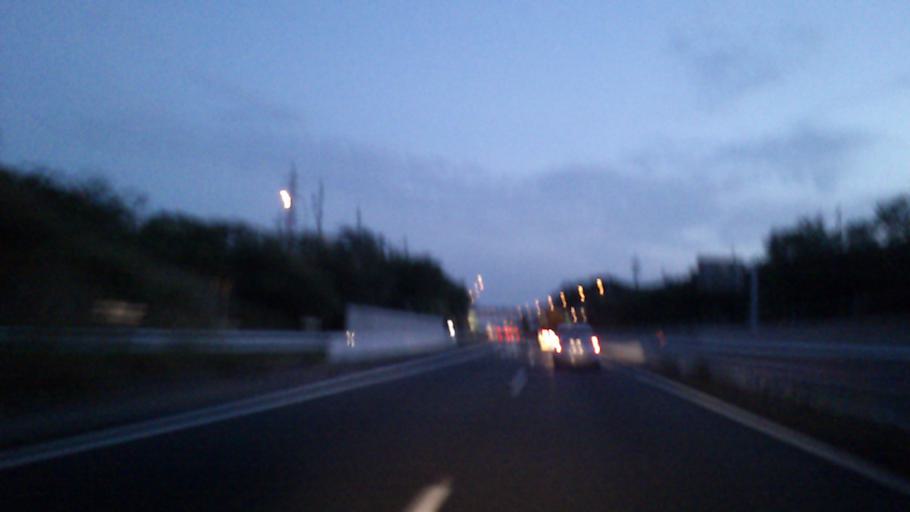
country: JP
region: Aichi
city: Kasugai
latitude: 35.2920
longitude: 136.9837
